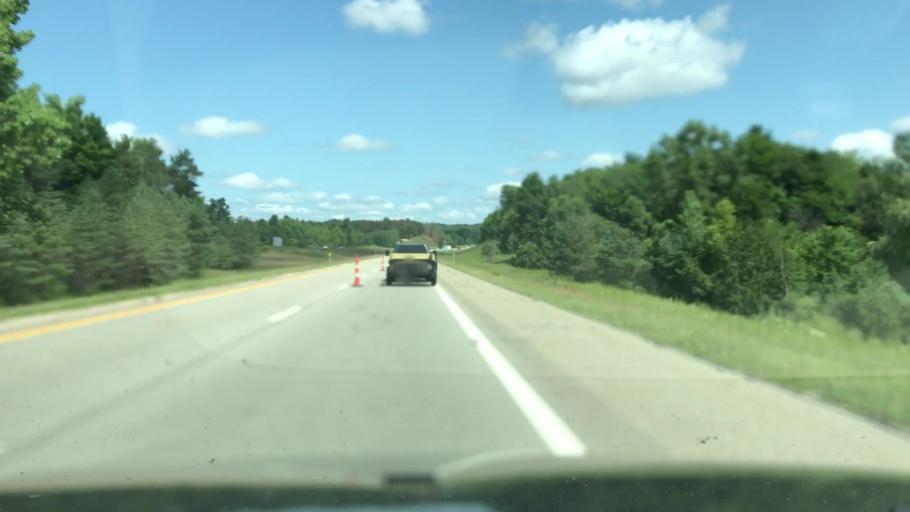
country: US
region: Michigan
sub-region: Mecosta County
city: Big Rapids
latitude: 43.7599
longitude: -85.5314
